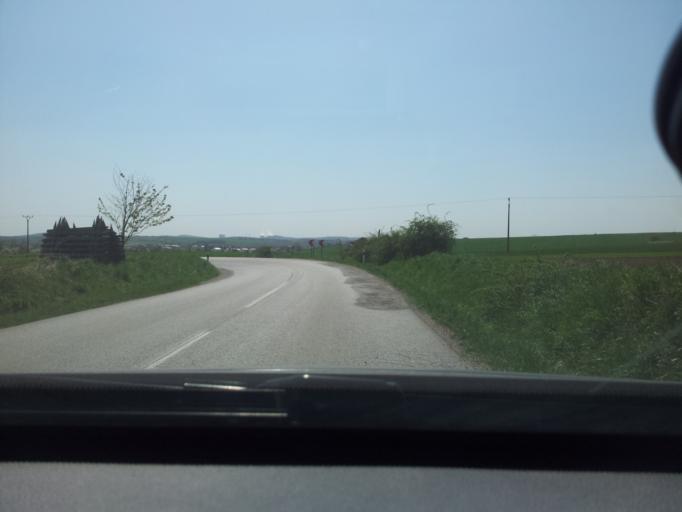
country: SK
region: Nitriansky
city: Zlate Moravce
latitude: 48.3638
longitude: 18.4098
